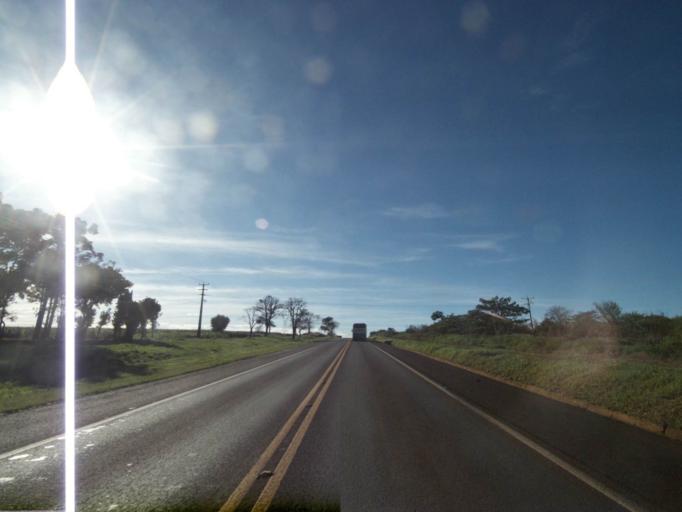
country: BR
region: Parana
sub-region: Cascavel
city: Cascavel
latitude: -25.0295
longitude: -53.5750
